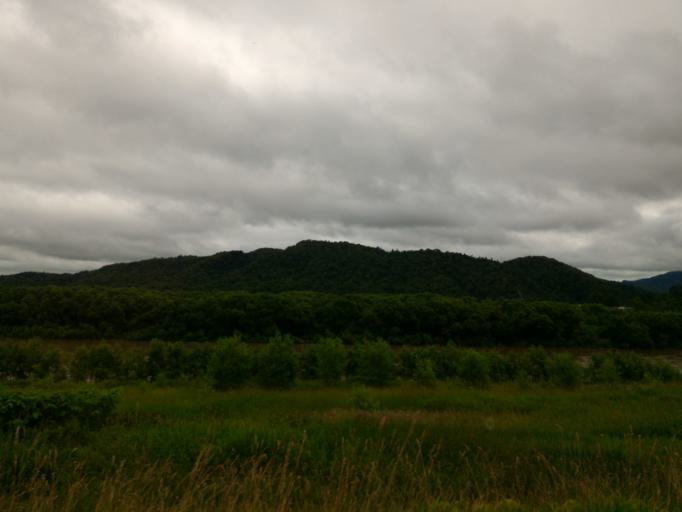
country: JP
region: Hokkaido
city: Nayoro
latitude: 44.7769
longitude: 142.0604
